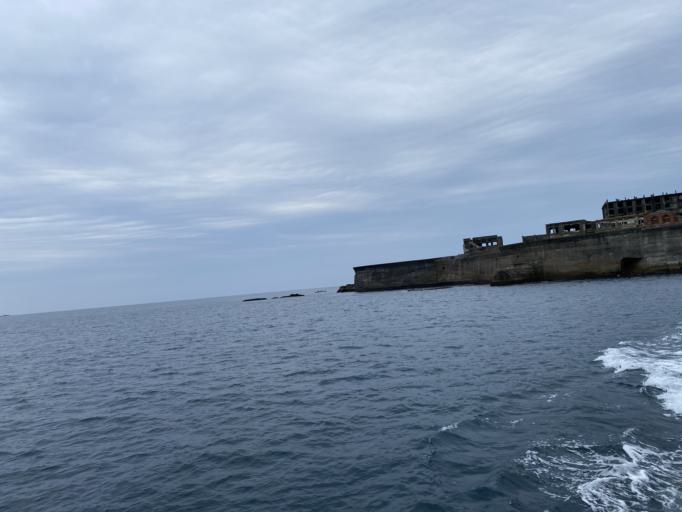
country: JP
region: Nagasaki
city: Nagasaki-shi
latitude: 32.6252
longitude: 129.7390
